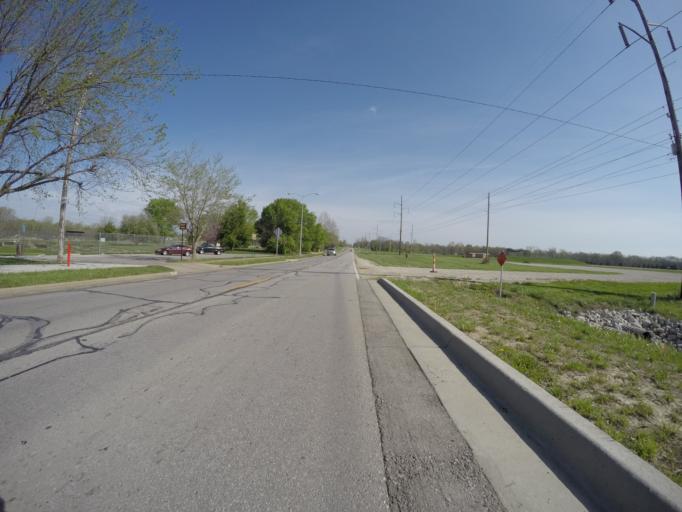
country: US
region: Missouri
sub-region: Jackson County
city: Grandview
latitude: 38.8741
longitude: -94.5083
